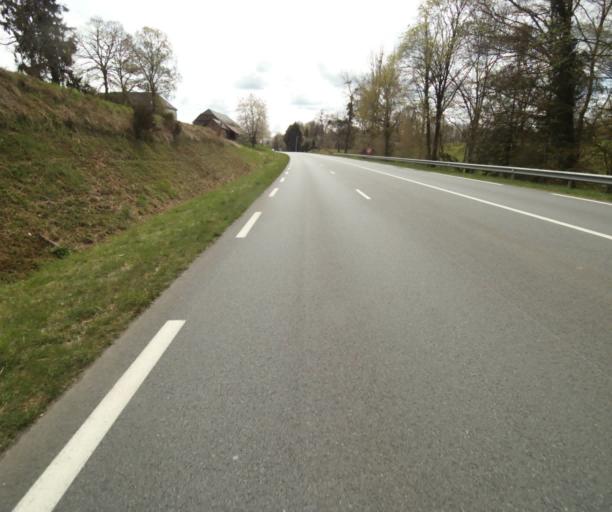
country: FR
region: Limousin
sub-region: Departement de la Correze
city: Sainte-Fortunade
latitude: 45.2076
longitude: 1.8265
